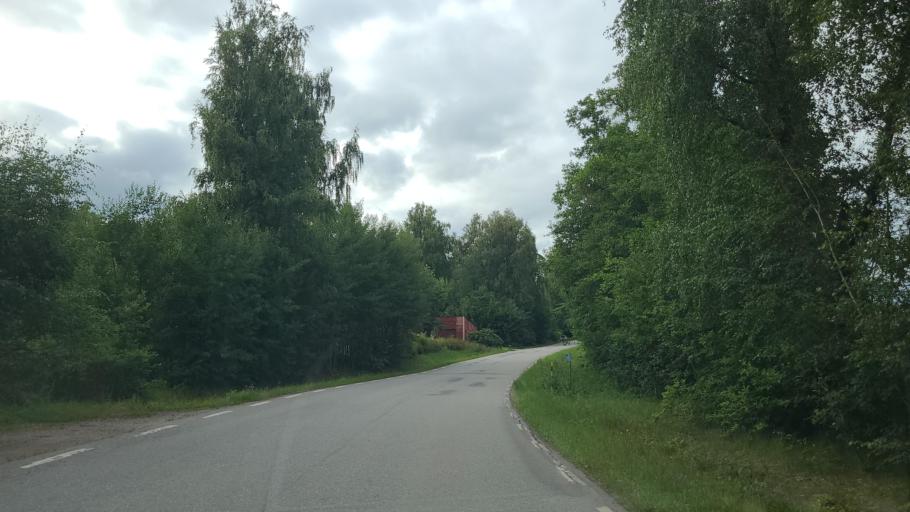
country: SE
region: Stockholm
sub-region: Upplands-Bro Kommun
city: Bro
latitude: 59.4964
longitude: 17.5698
